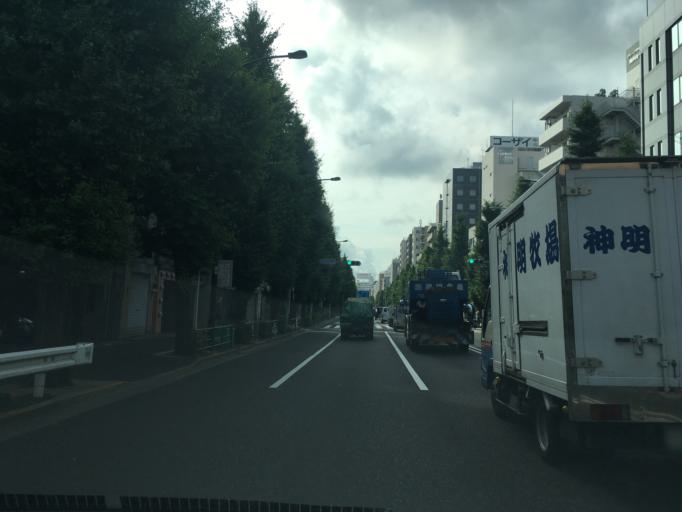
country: JP
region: Tokyo
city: Tokyo
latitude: 35.7008
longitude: 139.6323
